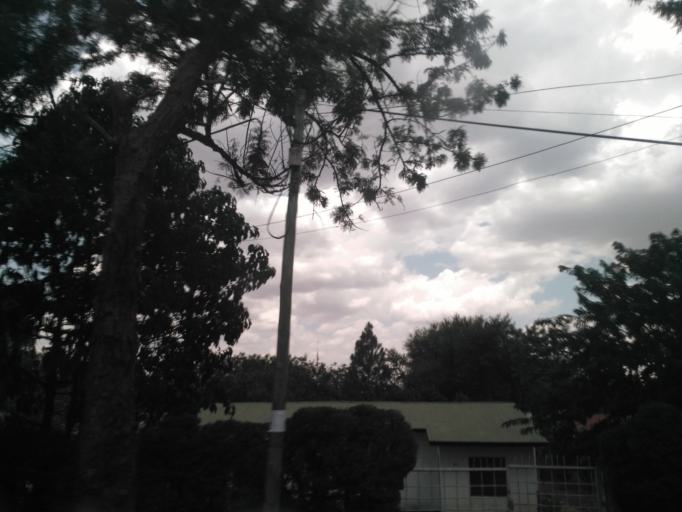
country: TZ
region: Mwanza
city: Mwanza
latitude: -2.5282
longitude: 32.8936
